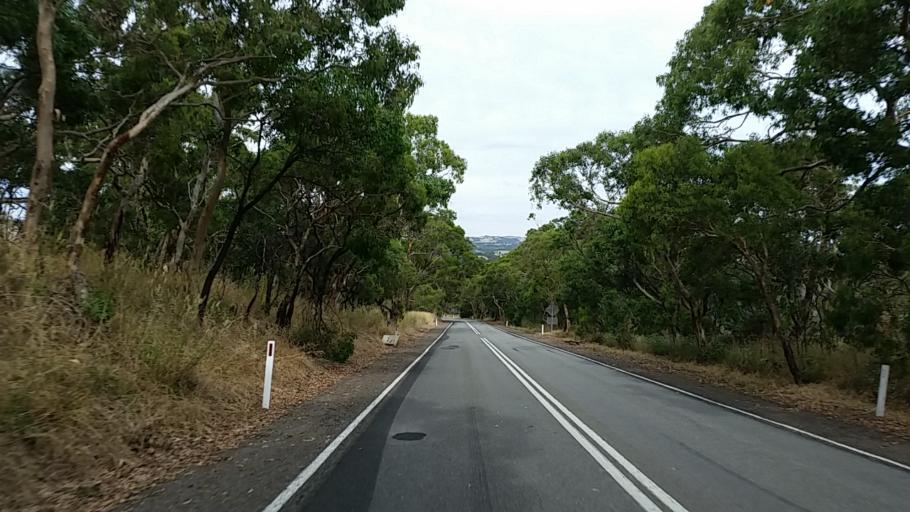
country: AU
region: South Australia
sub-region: Onkaparinga
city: Aldinga
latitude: -35.3775
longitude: 138.4595
